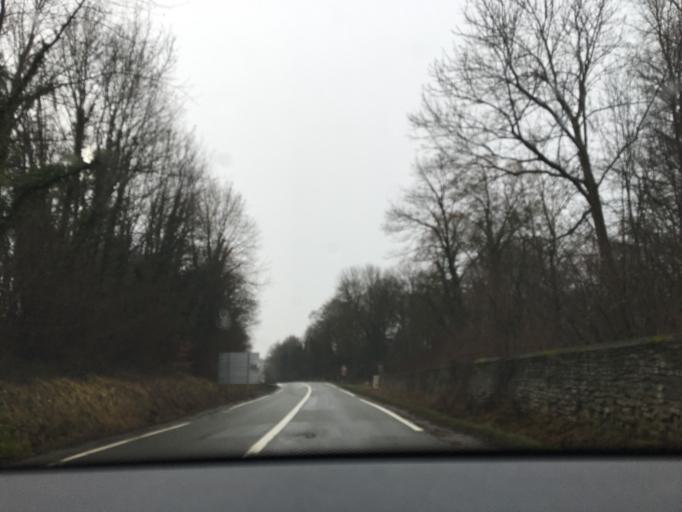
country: FR
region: Ile-de-France
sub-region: Departement des Yvelines
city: Follainville-Dennemont
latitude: 49.0316
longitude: 1.7468
